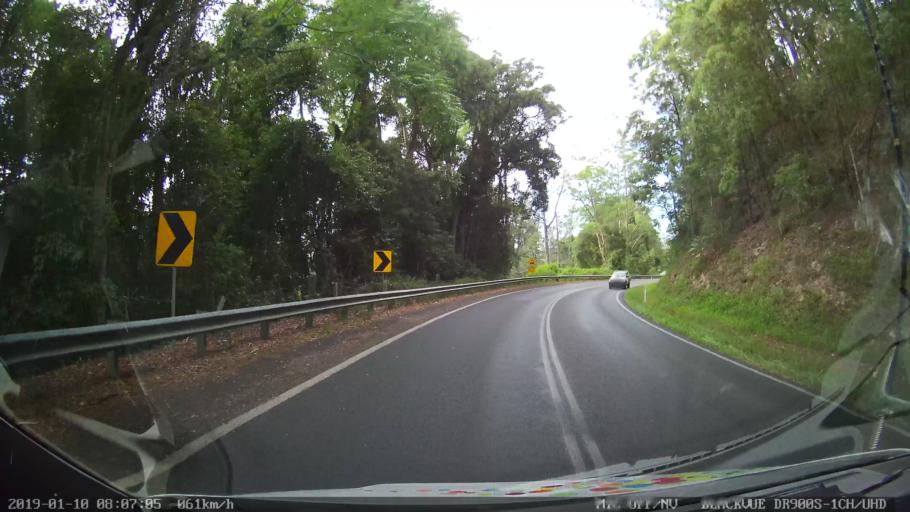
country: AU
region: New South Wales
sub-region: Bellingen
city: Bellingen
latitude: -30.4272
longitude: 152.8514
